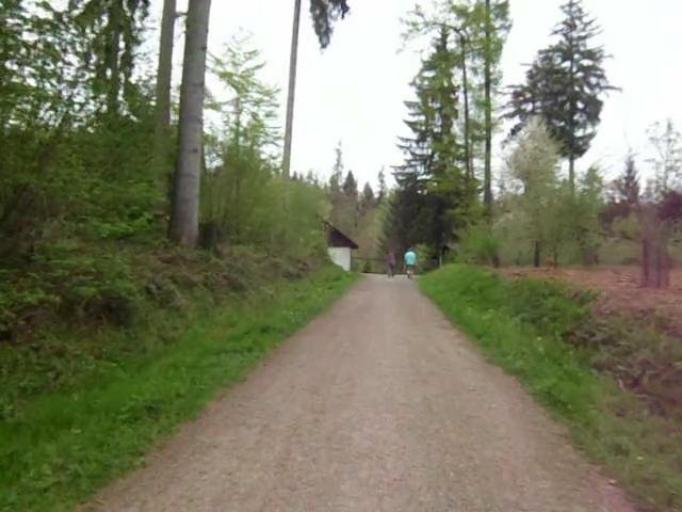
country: CH
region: Zurich
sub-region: Bezirk Hinwil
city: Rueti / Westlicher Dorfteil
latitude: 47.2558
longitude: 8.8372
